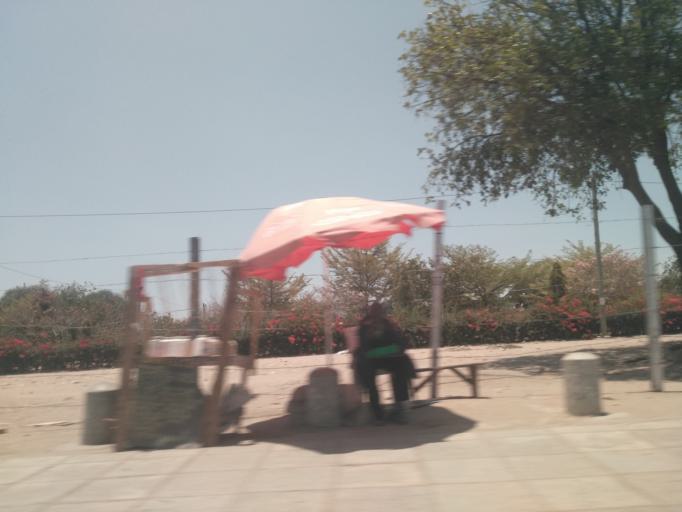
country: TZ
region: Dodoma
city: Dodoma
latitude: -6.1819
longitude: 35.7506
